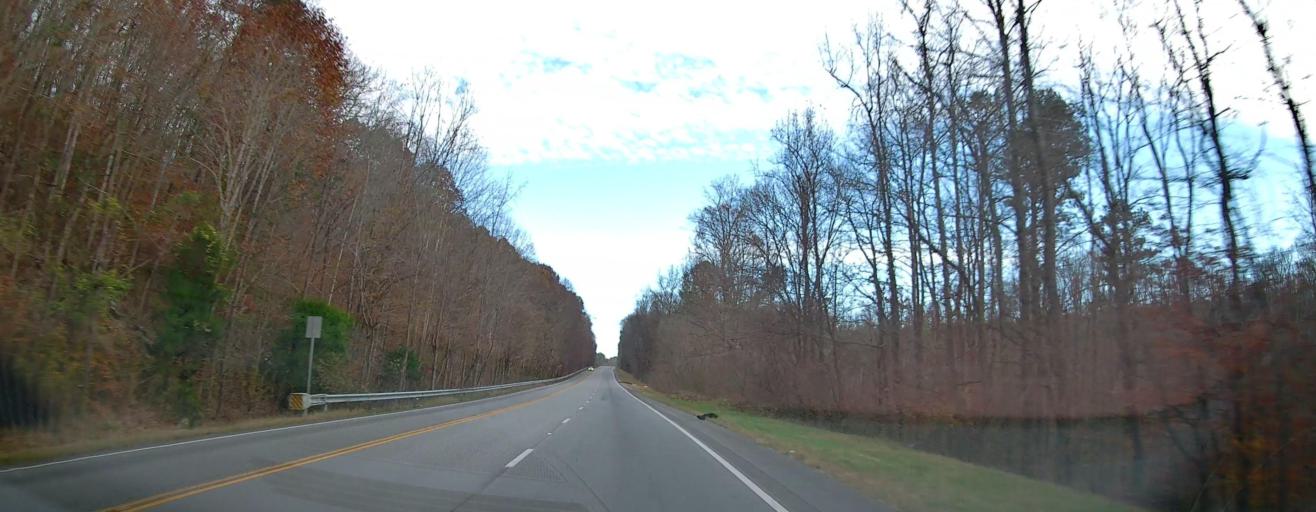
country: US
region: Alabama
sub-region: Marshall County
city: Arab
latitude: 34.3614
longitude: -86.6309
